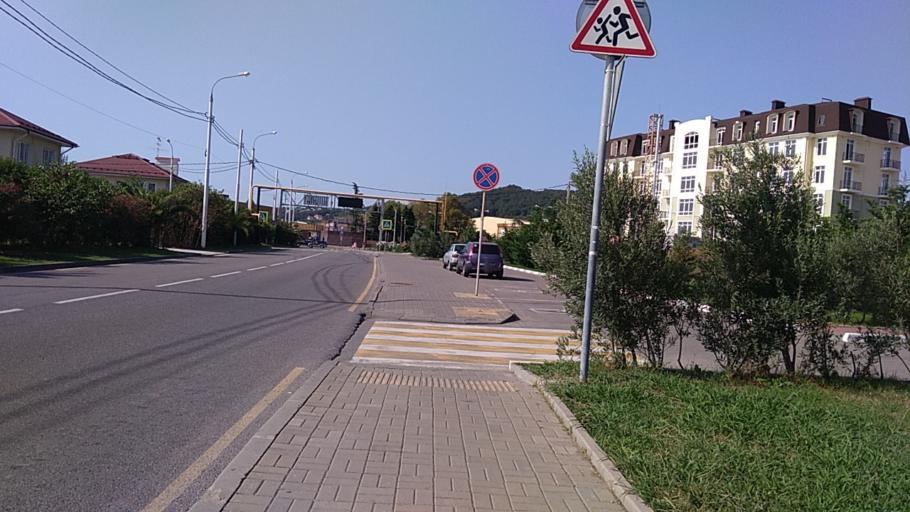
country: RU
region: Krasnodarskiy
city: Vysokoye
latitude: 43.3970
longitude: 39.9960
